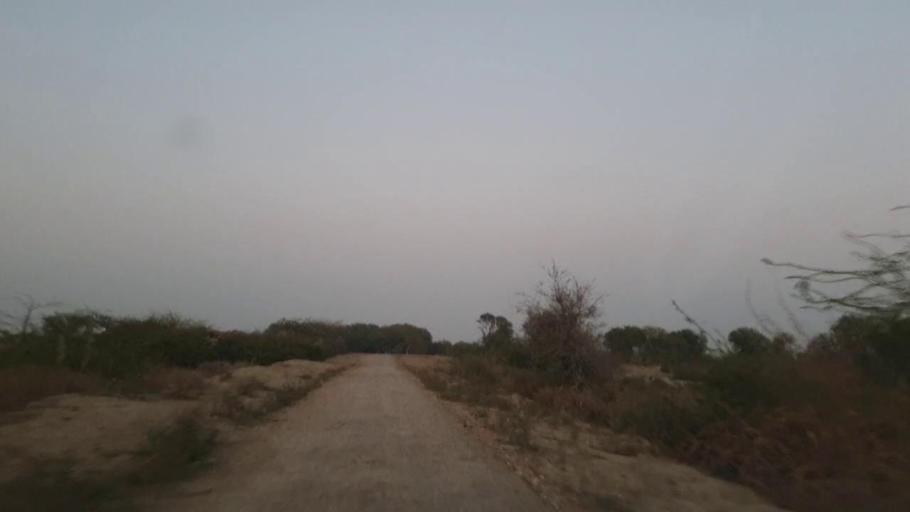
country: PK
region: Sindh
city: Bandhi
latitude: 26.6280
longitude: 68.3967
